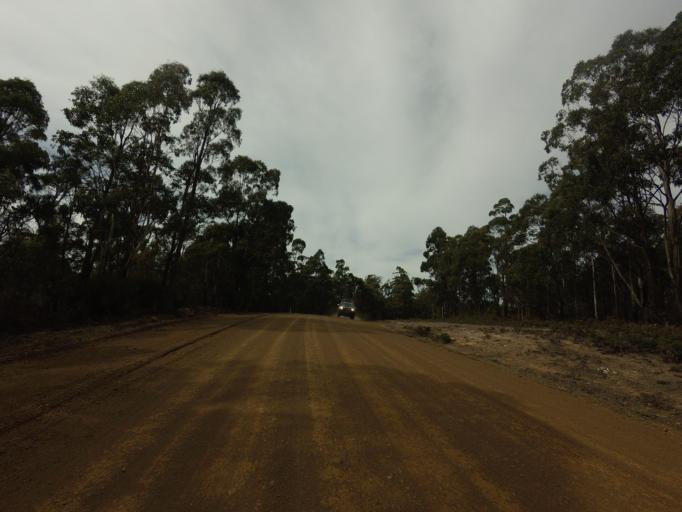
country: AU
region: Tasmania
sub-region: Sorell
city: Sorell
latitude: -42.5020
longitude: 147.6342
